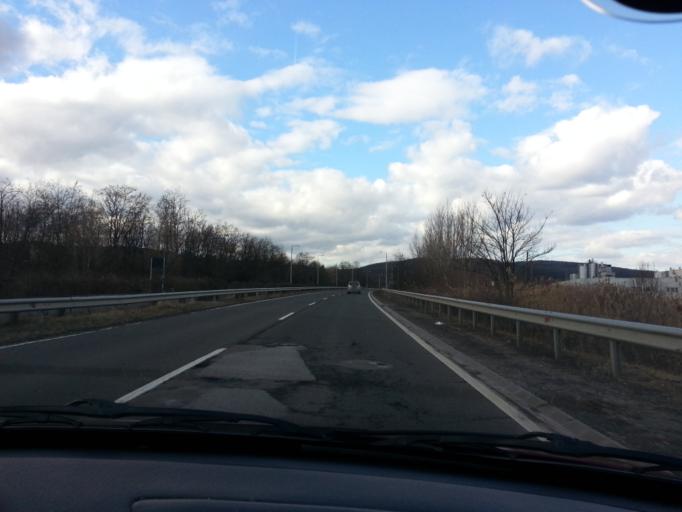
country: HU
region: Nograd
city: Salgotarjan
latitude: 48.0456
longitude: 19.7876
